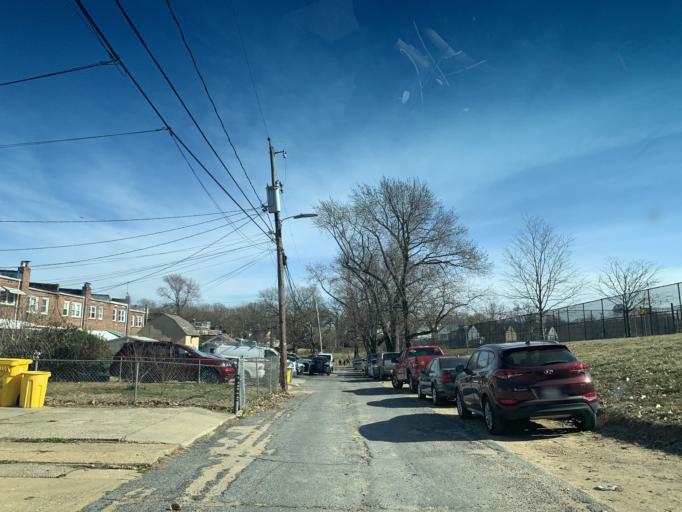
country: US
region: Maryland
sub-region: Anne Arundel County
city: Brooklyn Park
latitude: 39.2304
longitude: -76.6213
